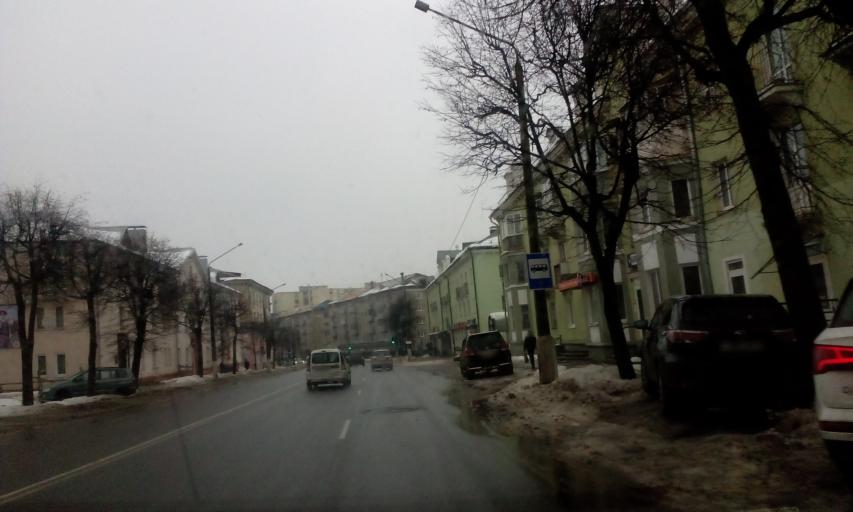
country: BY
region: Mogilev
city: Mahilyow
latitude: 53.9023
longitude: 30.3433
